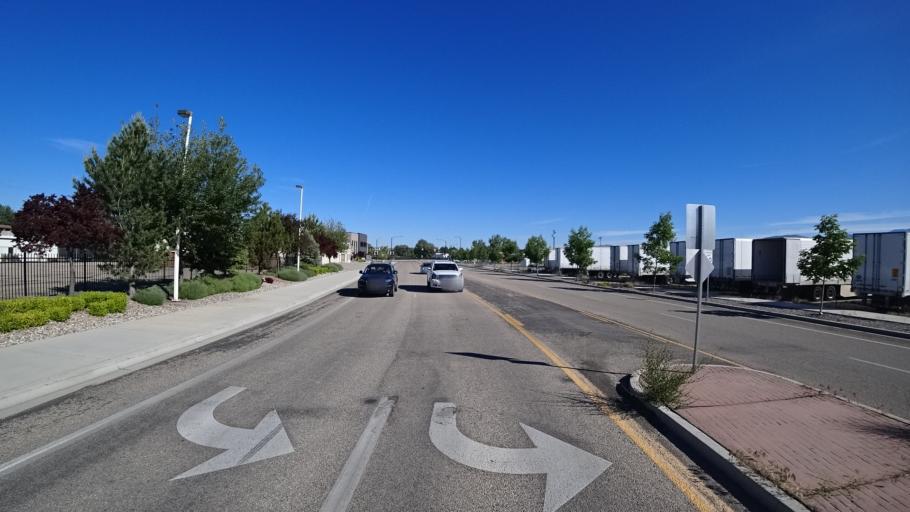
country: US
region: Idaho
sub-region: Ada County
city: Garden City
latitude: 43.6204
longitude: -116.2267
